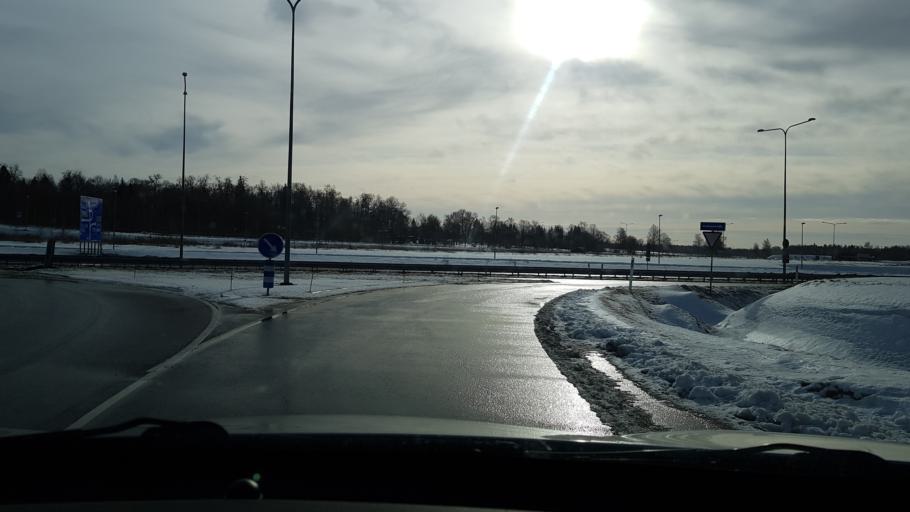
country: EE
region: Jaervamaa
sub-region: Paide linn
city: Paide
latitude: 58.9165
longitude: 25.6084
